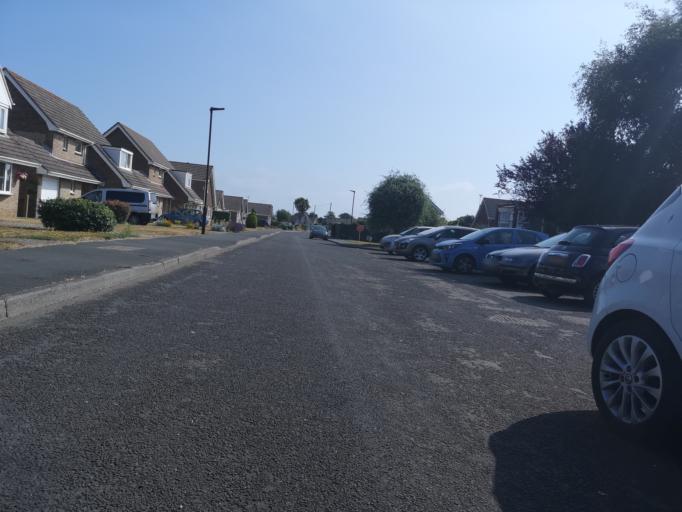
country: GB
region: England
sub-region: Isle of Wight
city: Bembridge
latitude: 50.6835
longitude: -1.0837
